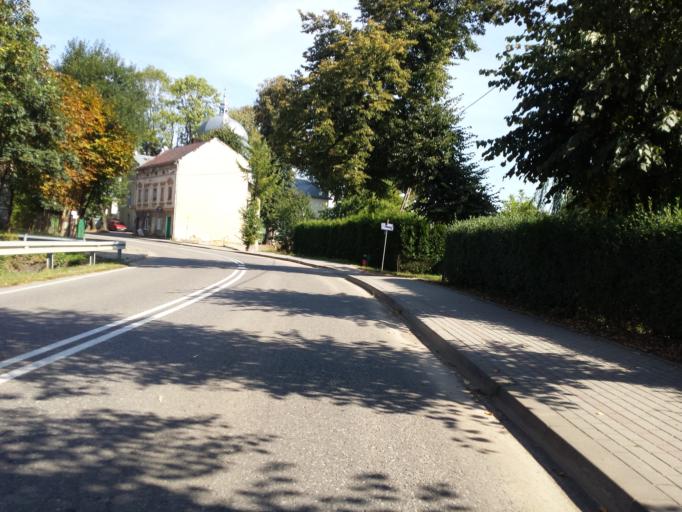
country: PL
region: Subcarpathian Voivodeship
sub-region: Powiat leski
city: Baligrod
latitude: 49.3351
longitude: 22.2873
